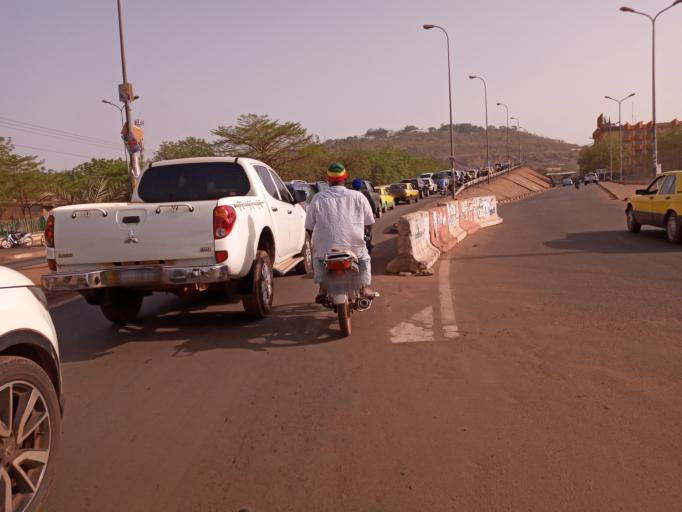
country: ML
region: Bamako
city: Bamako
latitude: 12.6467
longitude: -8.0096
